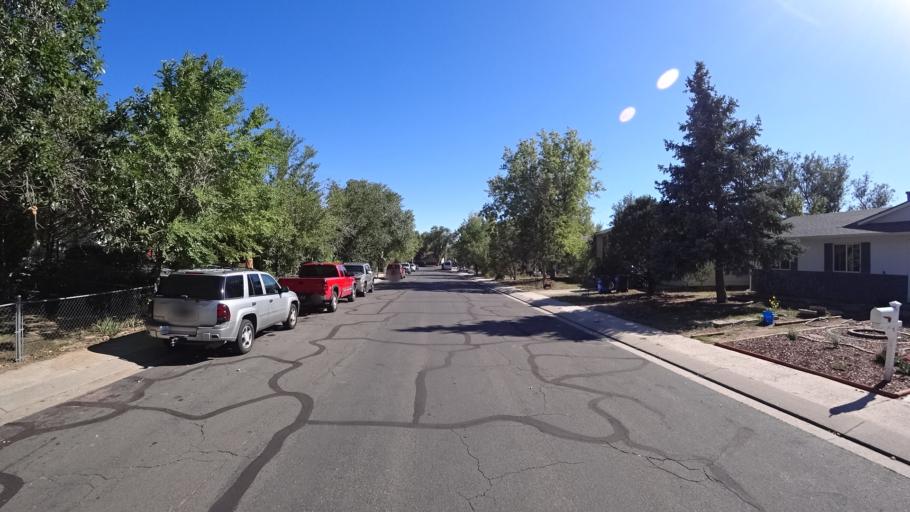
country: US
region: Colorado
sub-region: El Paso County
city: Stratmoor
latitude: 38.7964
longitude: -104.7461
